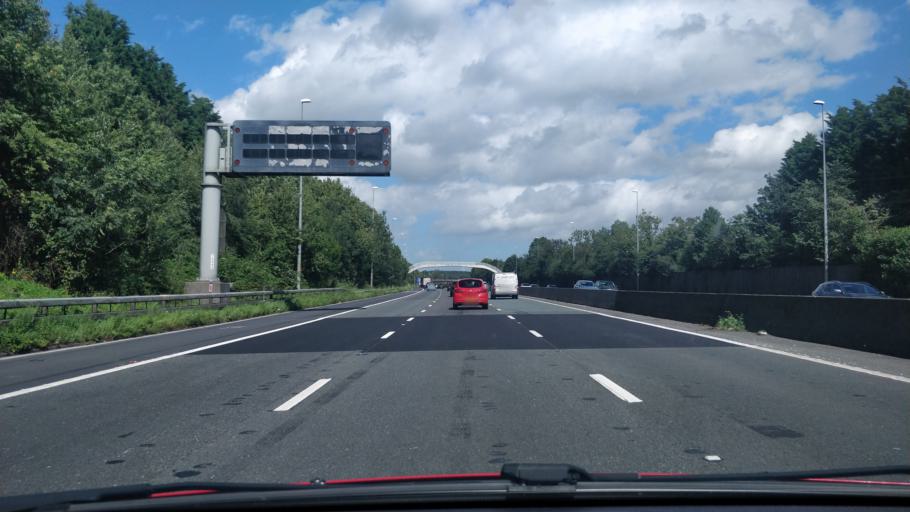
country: GB
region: England
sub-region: Borough of Wigan
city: Shevington
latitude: 53.5654
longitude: -2.6998
